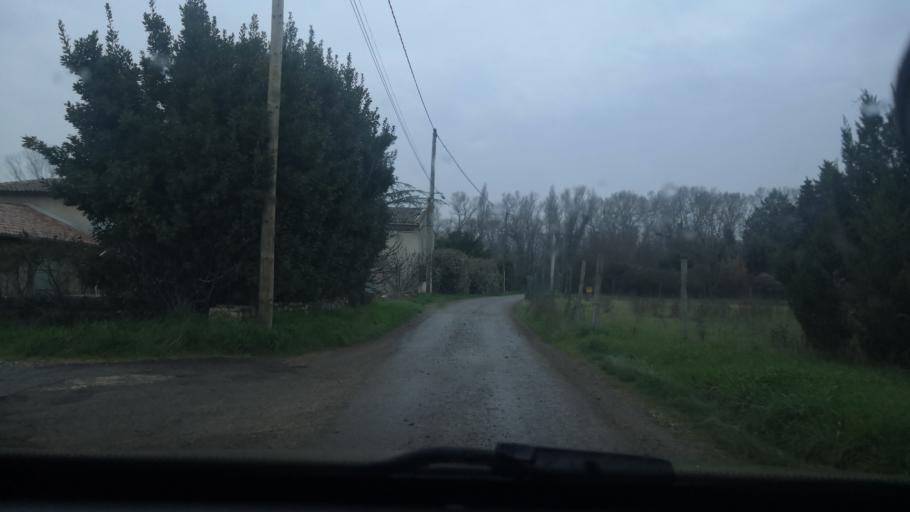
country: FR
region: Rhone-Alpes
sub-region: Departement de la Drome
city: Saint-Marcel-les-Sauzet
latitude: 44.5866
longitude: 4.8138
